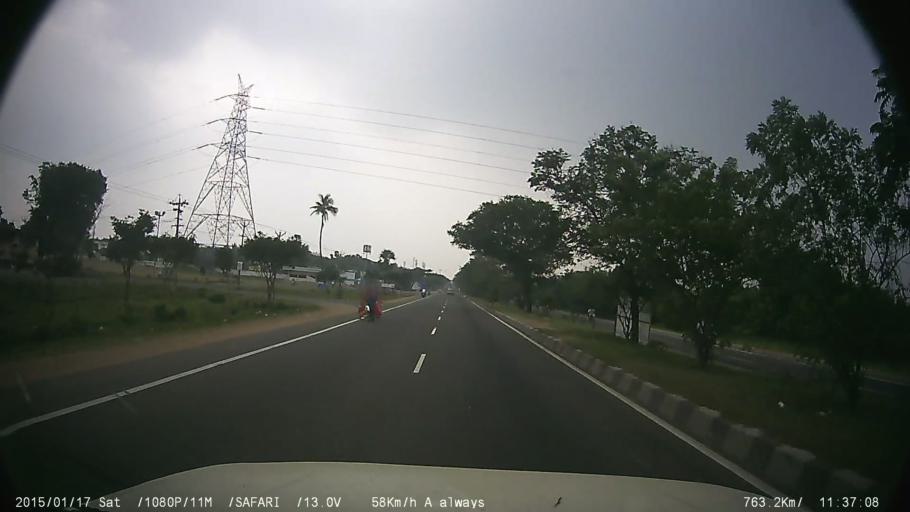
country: IN
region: Tamil Nadu
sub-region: Kancheepuram
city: Singapperumalkovil
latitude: 12.8048
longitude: 80.0266
